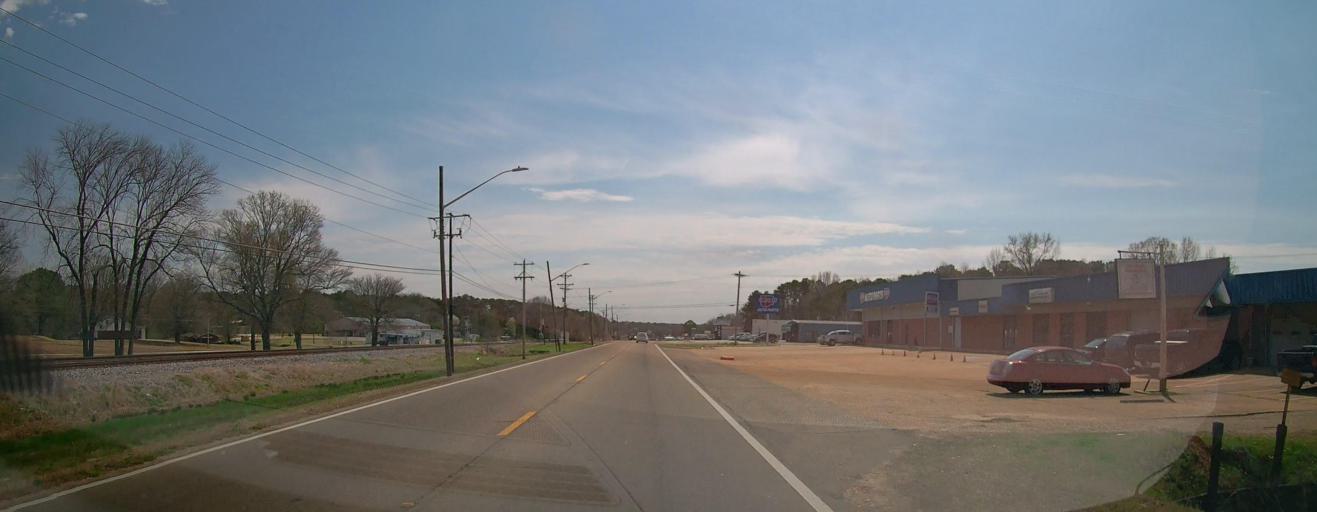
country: US
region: Mississippi
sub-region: Union County
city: New Albany
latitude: 34.5049
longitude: -89.0295
